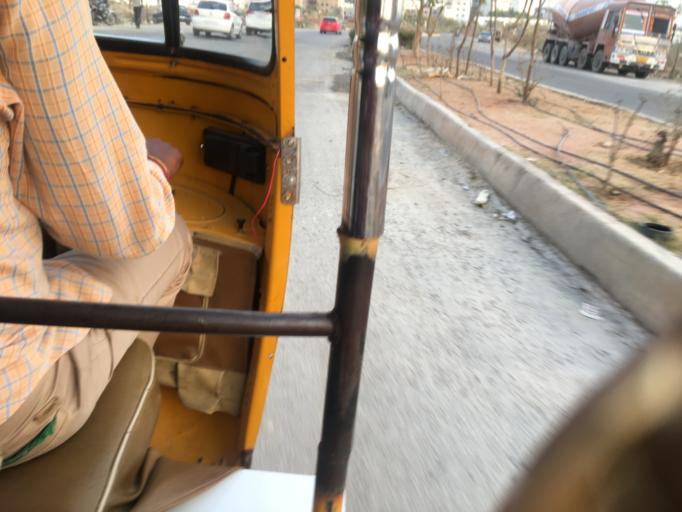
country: IN
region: Telangana
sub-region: Medak
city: Serilingampalle
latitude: 17.4322
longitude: 78.3309
